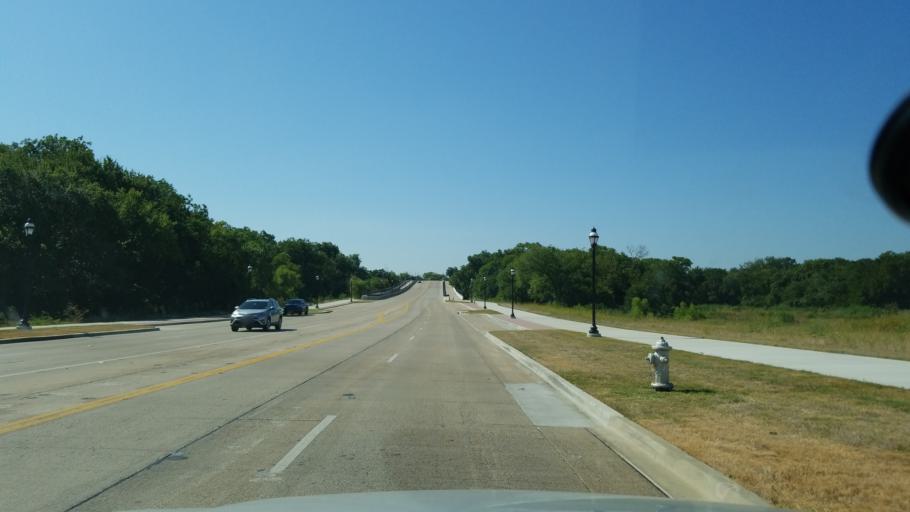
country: US
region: Texas
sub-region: Tarrant County
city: Mansfield
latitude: 32.5714
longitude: -97.1431
